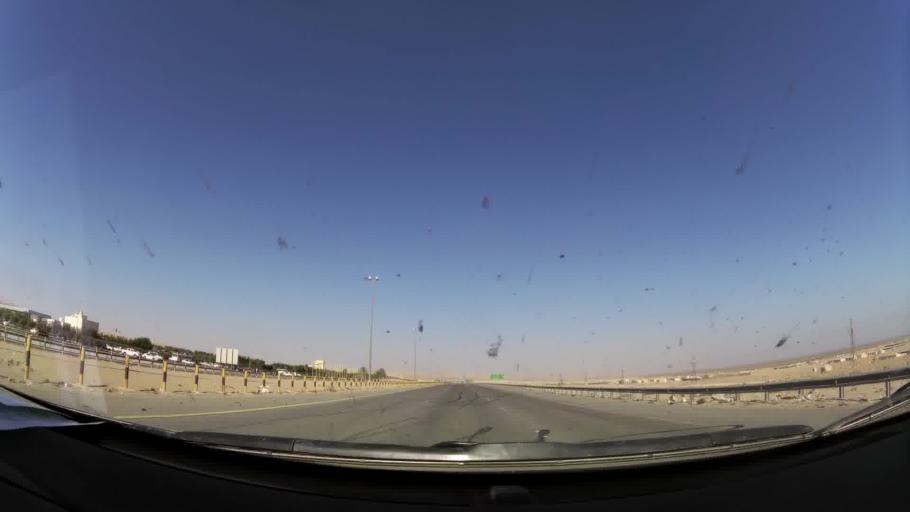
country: KW
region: Muhafazat al Jahra'
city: Al Jahra'
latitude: 29.4628
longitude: 47.7630
